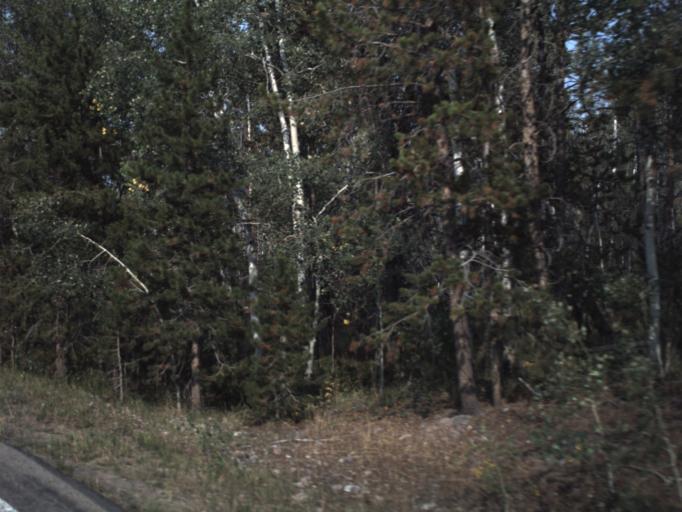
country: US
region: Wyoming
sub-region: Uinta County
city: Evanston
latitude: 40.9153
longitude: -110.8275
